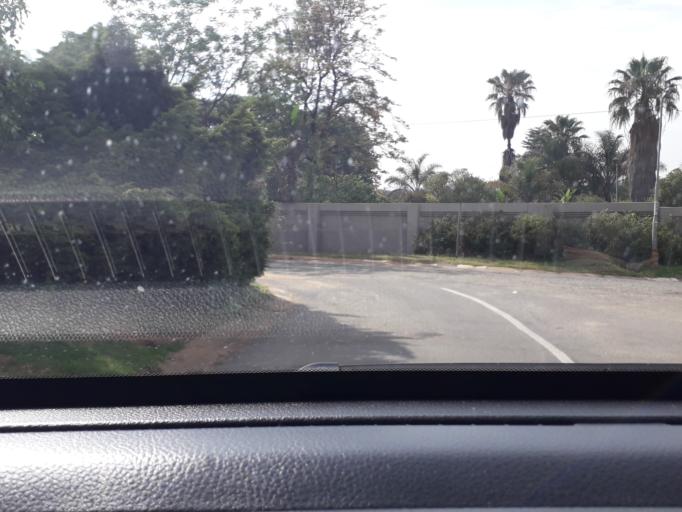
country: ZA
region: Gauteng
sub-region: City of Johannesburg Metropolitan Municipality
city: Modderfontein
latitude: -26.0911
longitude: 28.0631
